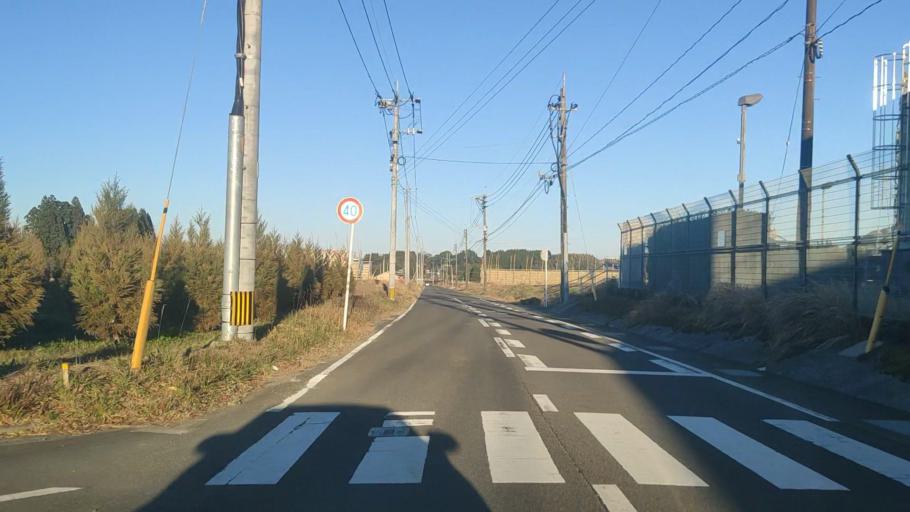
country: JP
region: Miyazaki
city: Miyazaki-shi
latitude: 31.8287
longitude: 131.3063
